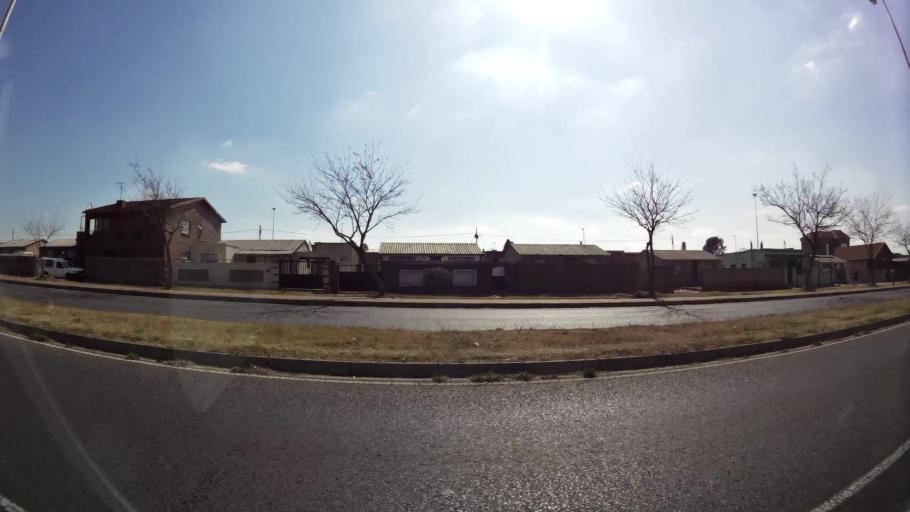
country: ZA
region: Gauteng
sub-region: City of Johannesburg Metropolitan Municipality
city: Soweto
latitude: -26.2764
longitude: 27.8678
